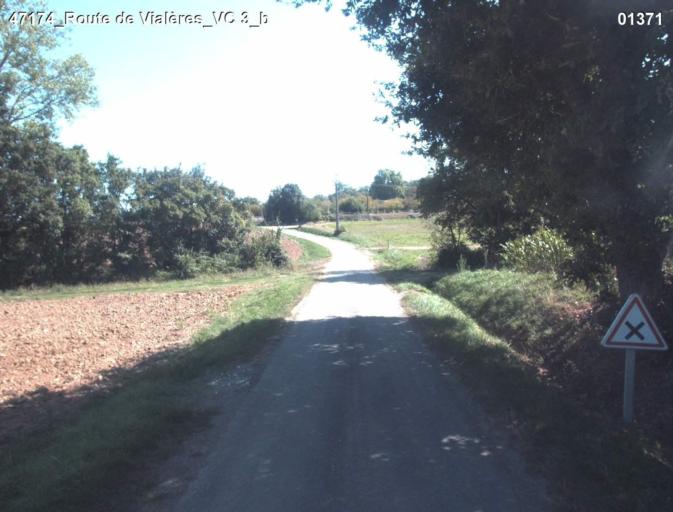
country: FR
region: Midi-Pyrenees
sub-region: Departement du Gers
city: Condom
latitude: 44.0458
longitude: 0.3788
